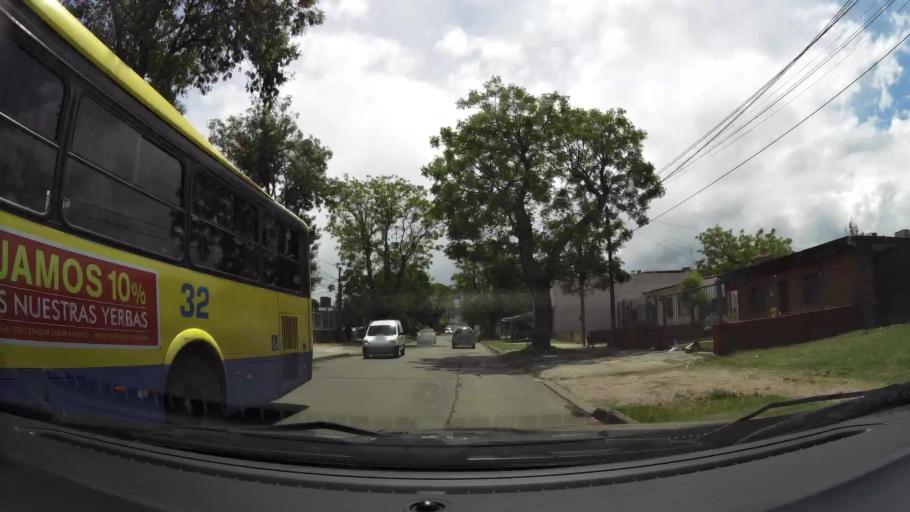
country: UY
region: Montevideo
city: Montevideo
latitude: -34.8770
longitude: -56.1267
